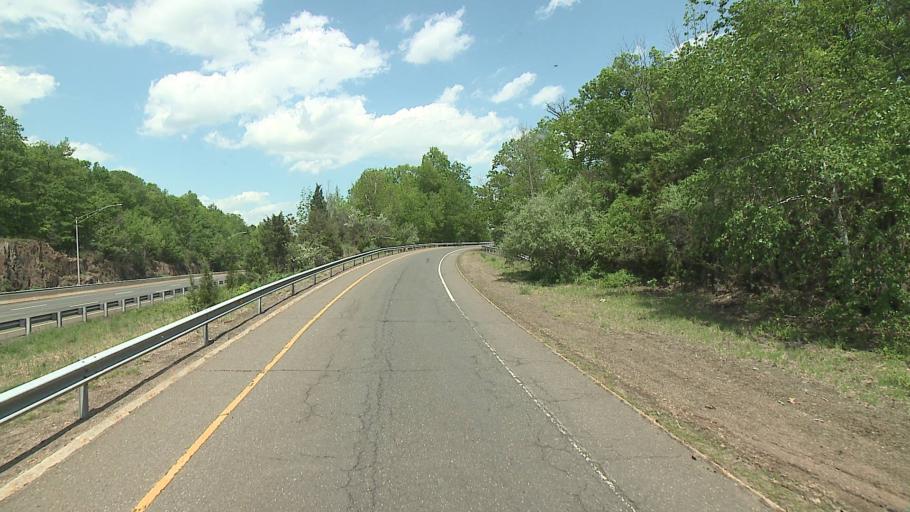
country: US
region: Connecticut
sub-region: Hartford County
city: Plainville
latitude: 41.6746
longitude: -72.8205
